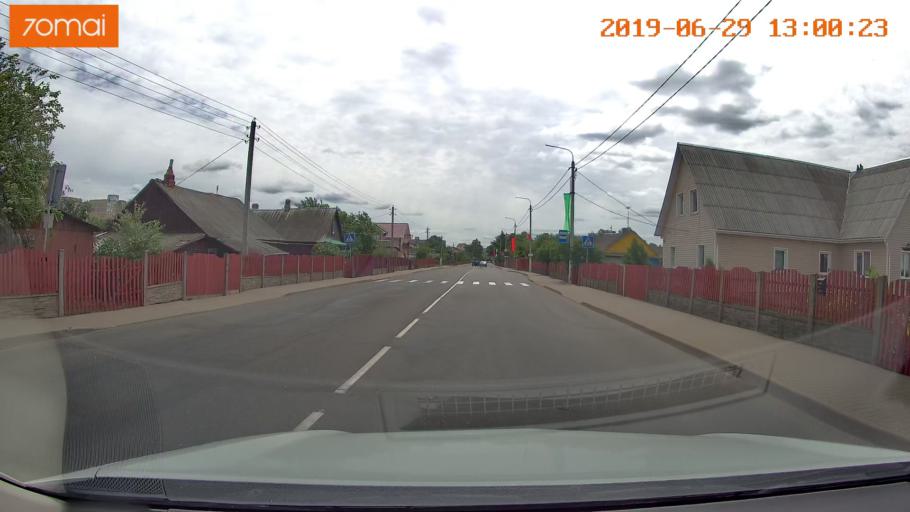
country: BY
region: Minsk
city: Slutsk
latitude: 53.0450
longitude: 27.5568
